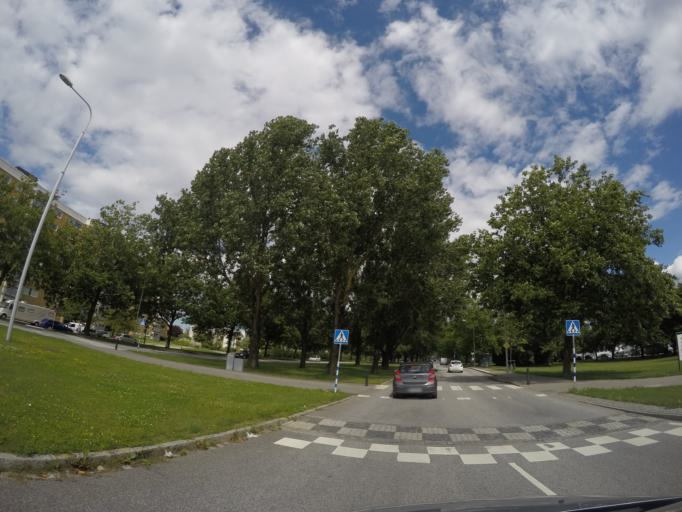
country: SE
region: Skane
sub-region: Malmo
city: Malmoe
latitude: 55.5753
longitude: 12.9919
